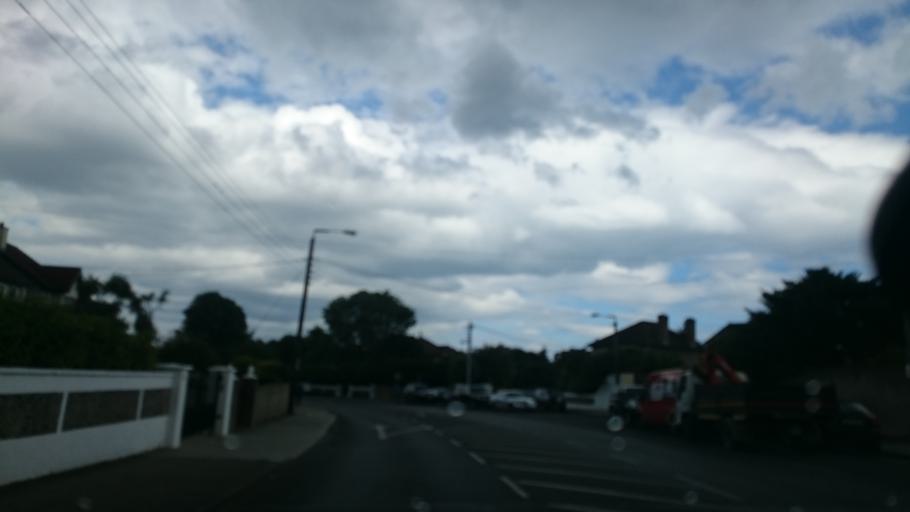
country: IE
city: Booterstown
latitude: 53.3005
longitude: -6.2016
